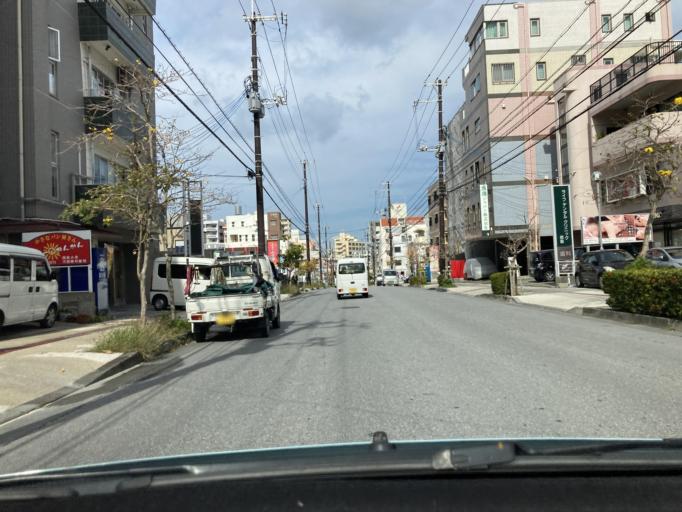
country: JP
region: Okinawa
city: Naha-shi
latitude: 26.2349
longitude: 127.6894
